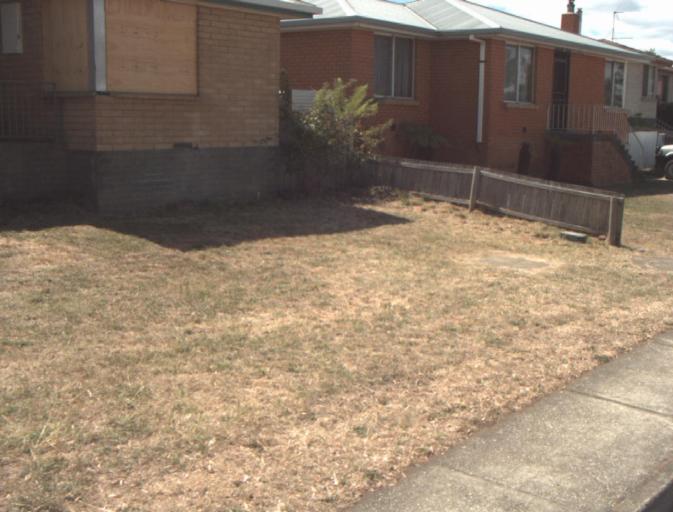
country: AU
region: Tasmania
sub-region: Launceston
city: Newstead
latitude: -41.4126
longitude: 147.1736
